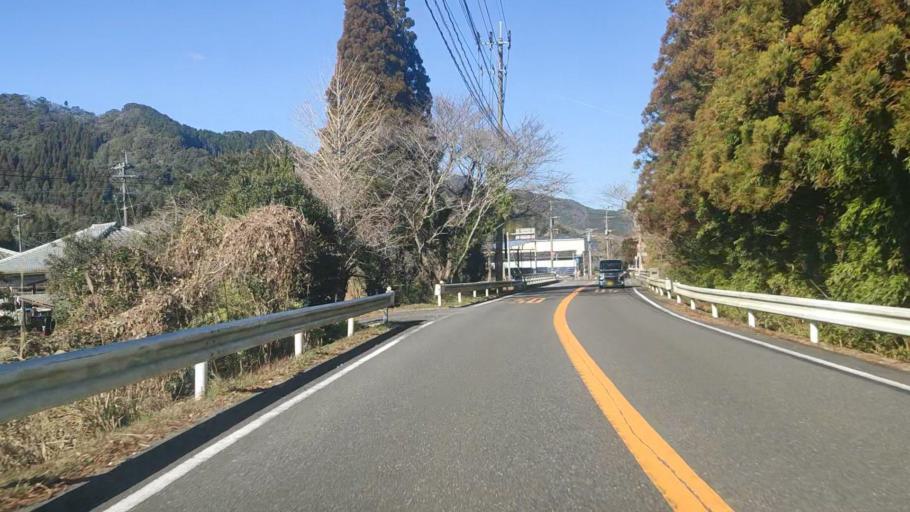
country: JP
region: Oita
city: Saiki
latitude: 32.9013
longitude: 131.9341
